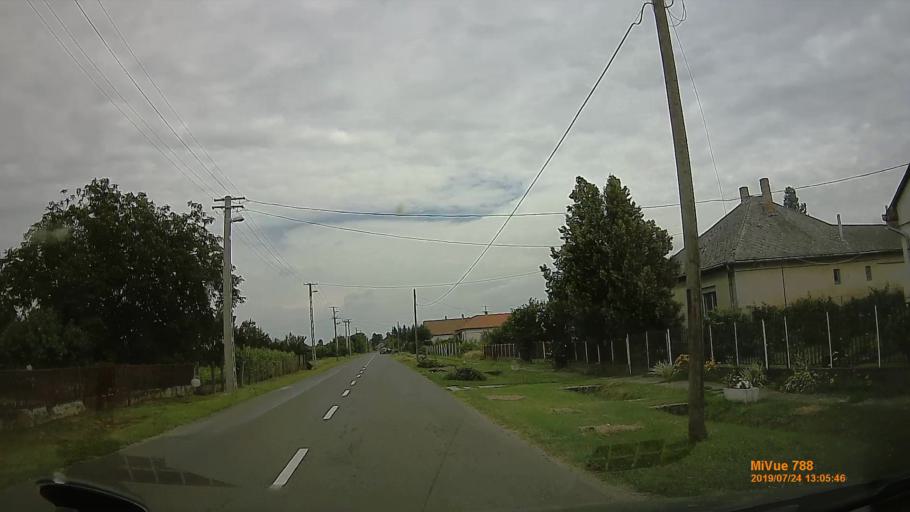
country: HU
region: Szabolcs-Szatmar-Bereg
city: Aranyosapati
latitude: 48.1943
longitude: 22.2971
